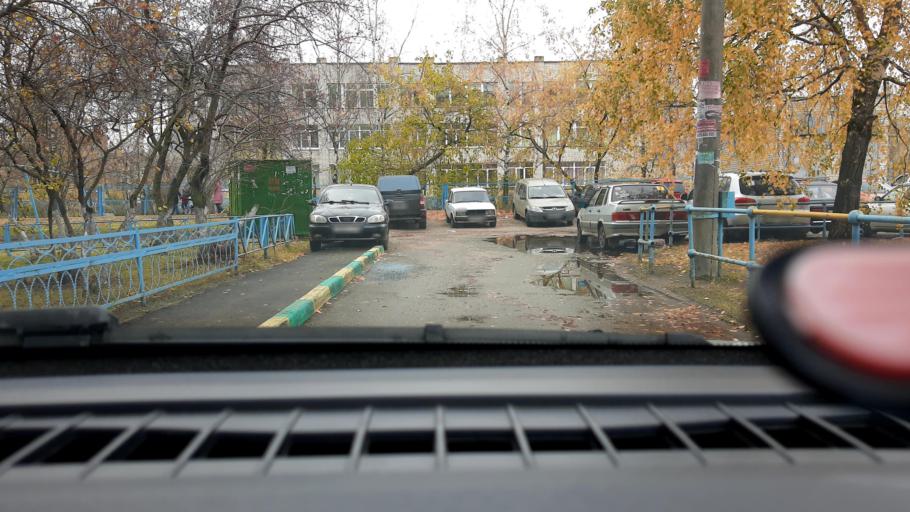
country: RU
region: Nizjnij Novgorod
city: Burevestnik
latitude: 56.2284
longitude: 43.8775
